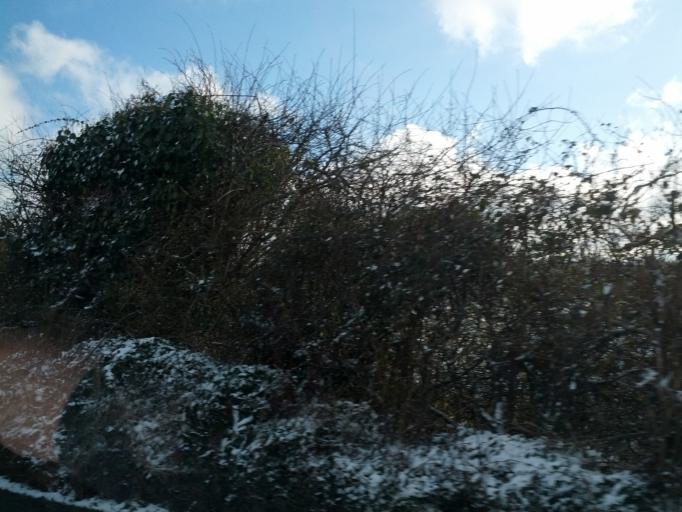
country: IE
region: Connaught
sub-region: County Galway
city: Gort
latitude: 53.1427
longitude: -8.9132
